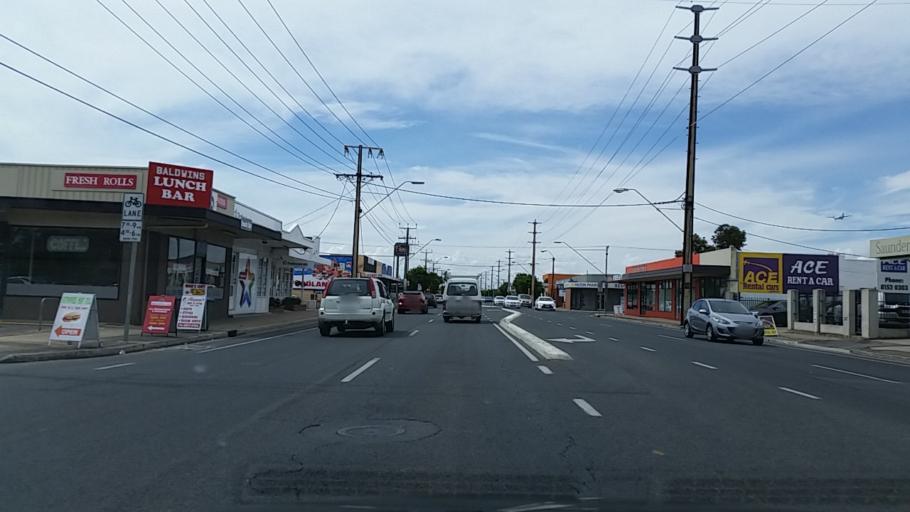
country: AU
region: South Australia
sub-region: City of West Torrens
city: Plympton
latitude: -34.9389
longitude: 138.5529
